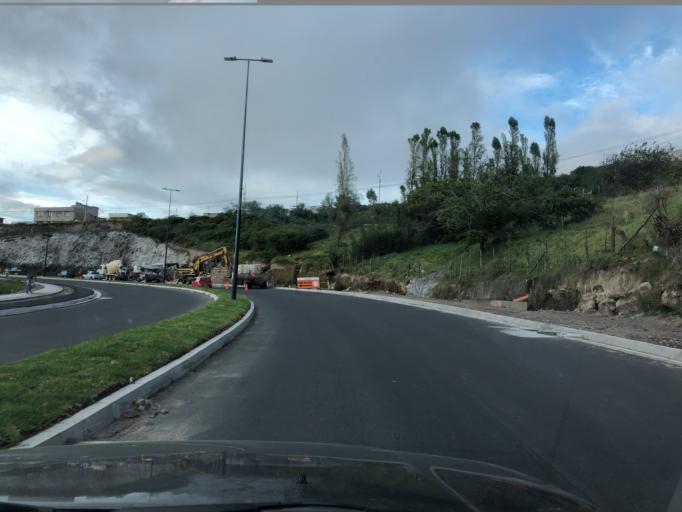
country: EC
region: Imbabura
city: Ibarra
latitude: 0.3479
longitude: -78.1419
